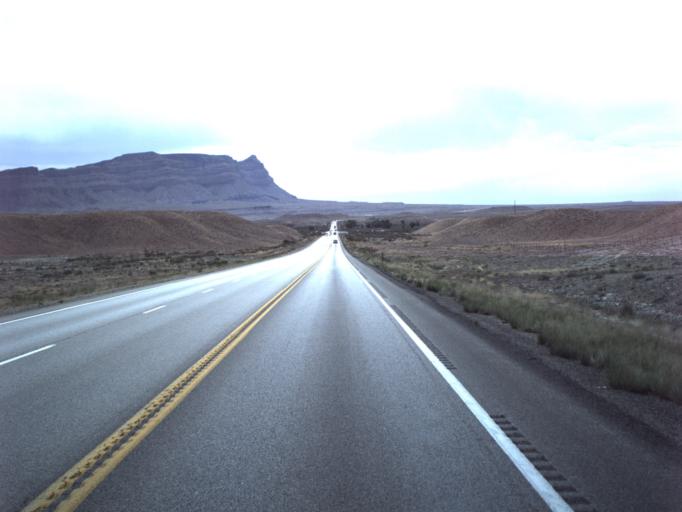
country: US
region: Utah
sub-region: Carbon County
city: East Carbon City
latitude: 39.2759
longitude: -110.3476
